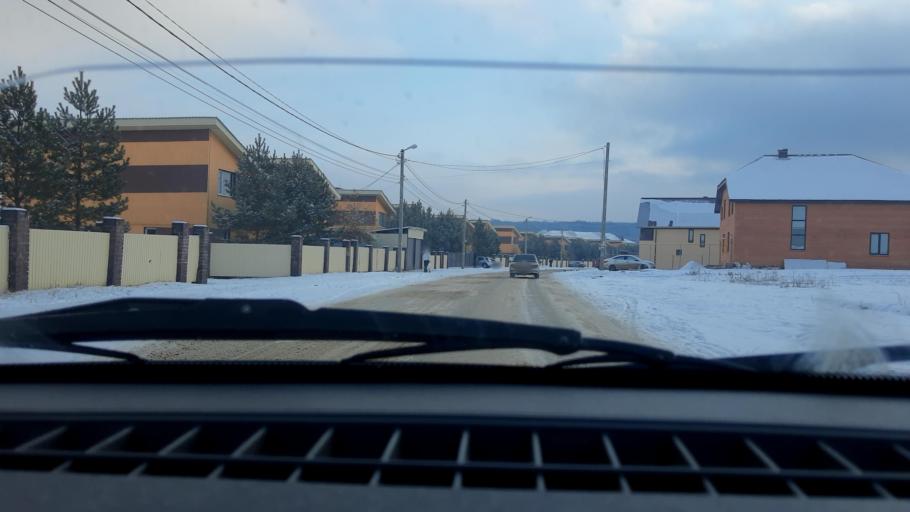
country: RU
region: Bashkortostan
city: Avdon
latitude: 54.4795
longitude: 55.8756
